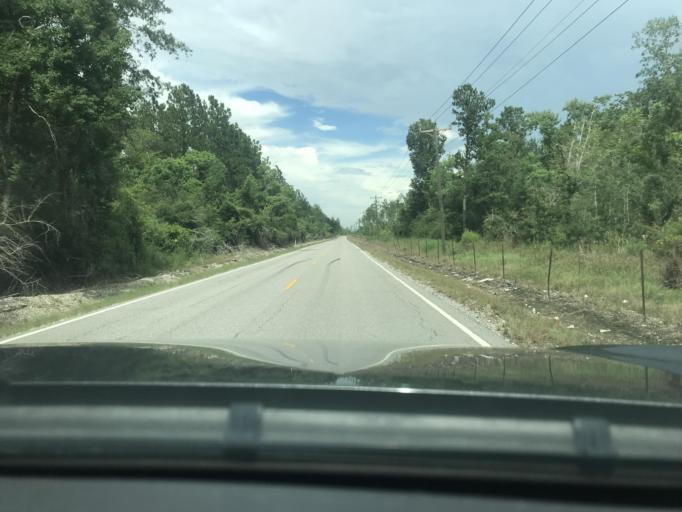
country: US
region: Louisiana
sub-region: Calcasieu Parish
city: Moss Bluff
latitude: 30.3885
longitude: -93.2397
